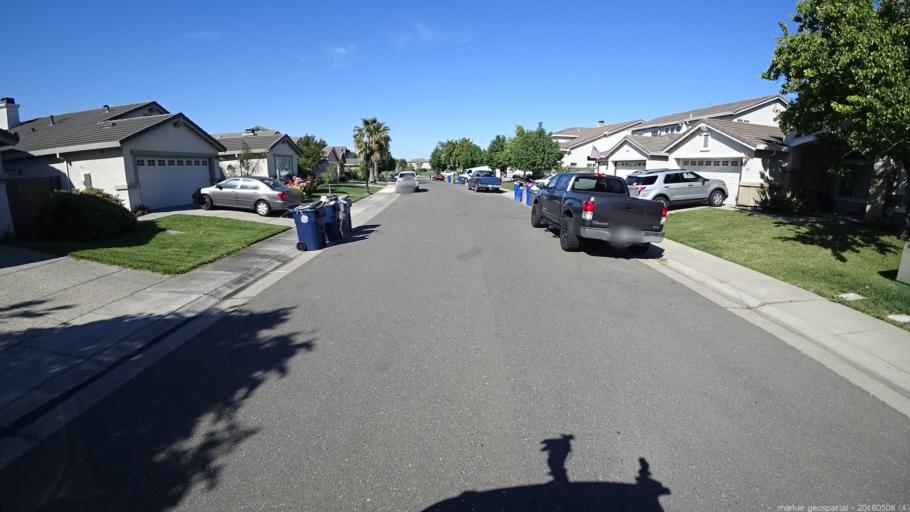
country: US
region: California
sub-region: Sacramento County
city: Elverta
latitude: 38.6783
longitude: -121.4983
